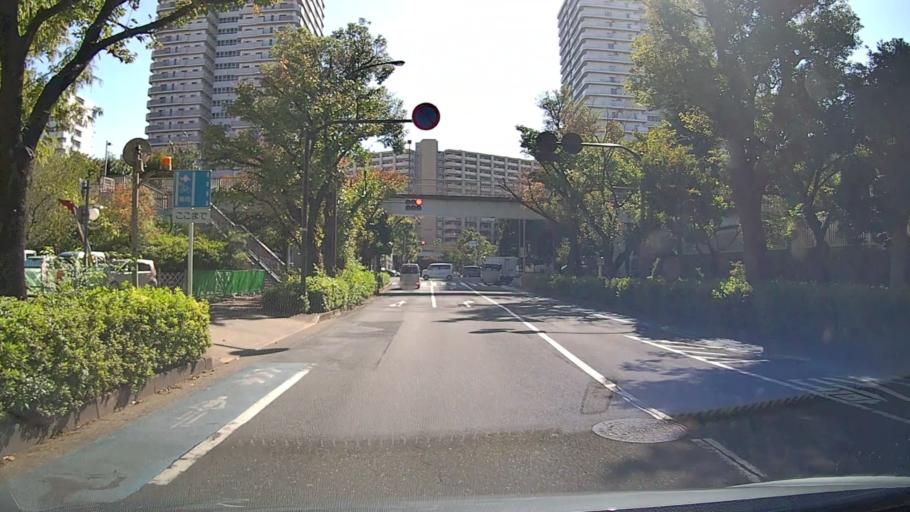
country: JP
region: Saitama
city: Wako
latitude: 35.7593
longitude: 139.6254
